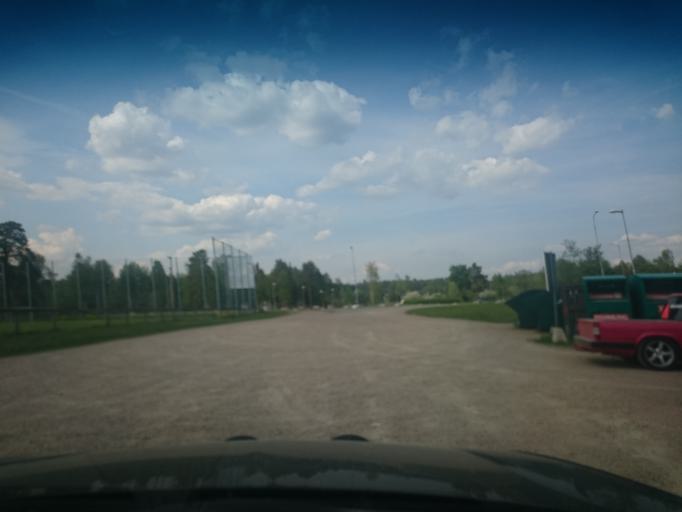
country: SE
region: Joenkoeping
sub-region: Vetlanda Kommun
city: Vetlanda
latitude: 57.4389
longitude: 15.0687
